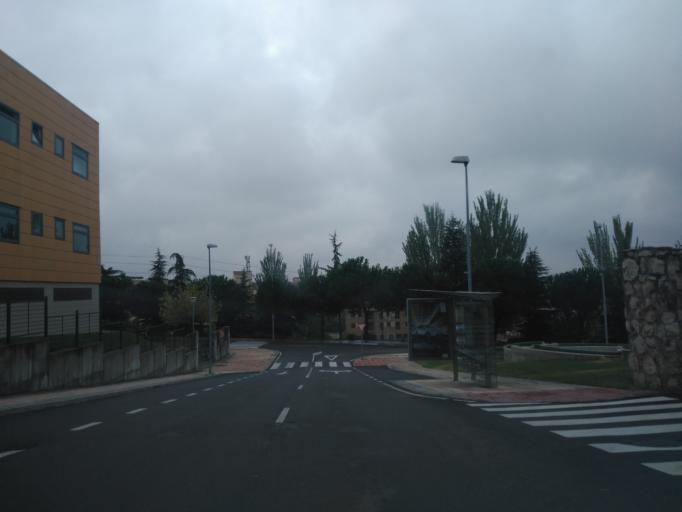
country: ES
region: Castille and Leon
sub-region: Provincia de Salamanca
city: Salamanca
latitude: 40.9529
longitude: -5.6797
